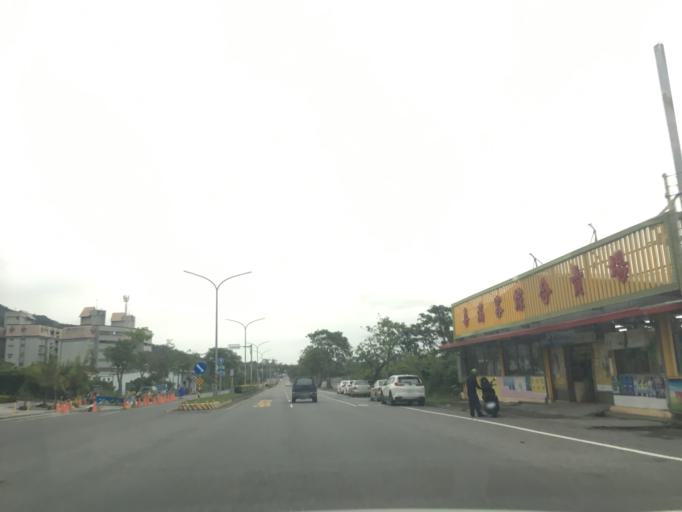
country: TW
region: Taiwan
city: Taitung City
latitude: 22.7073
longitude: 121.0424
